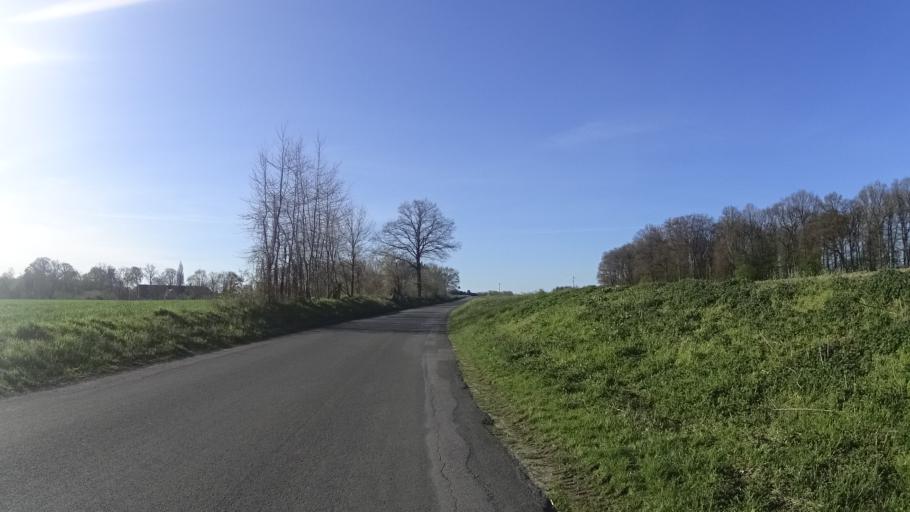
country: DE
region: North Rhine-Westphalia
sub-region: Regierungsbezirk Munster
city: Greven
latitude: 52.0742
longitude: 7.6082
